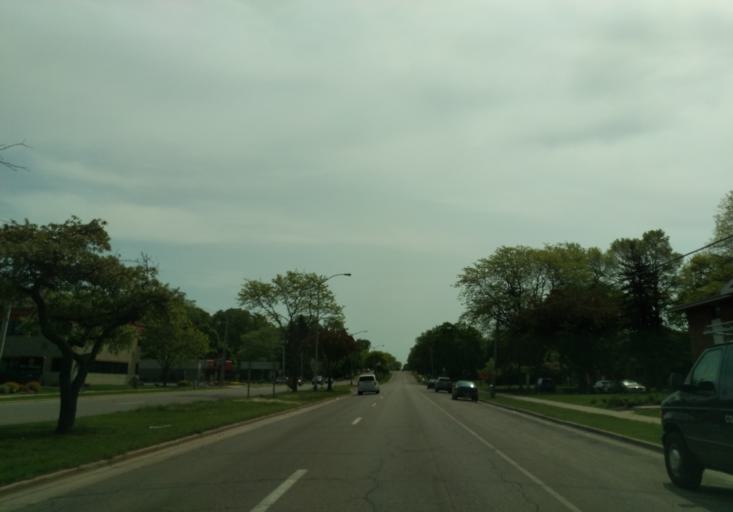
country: US
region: Wisconsin
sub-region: Dane County
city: Monona
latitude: 43.0842
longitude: -89.3007
